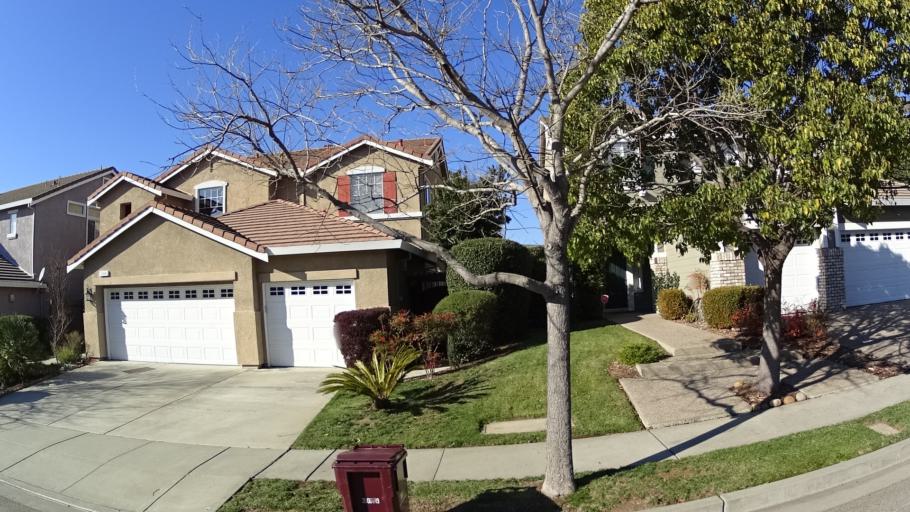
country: US
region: California
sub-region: Alameda County
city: Fairview
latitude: 37.6858
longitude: -122.0390
